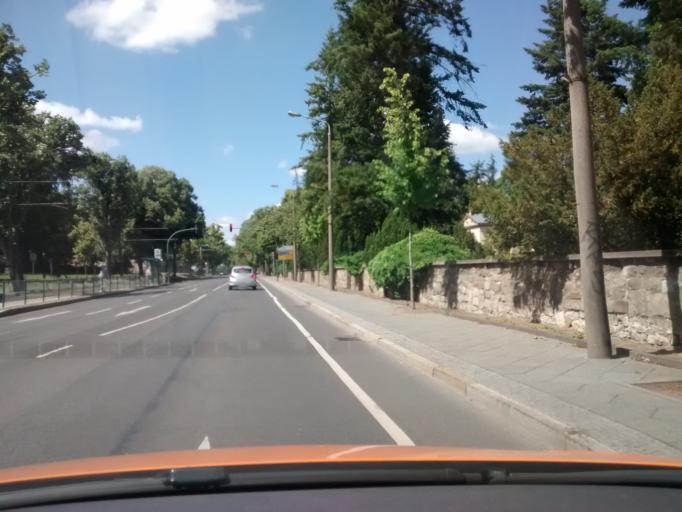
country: DE
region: Brandenburg
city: Potsdam
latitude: 52.3857
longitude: 13.0723
